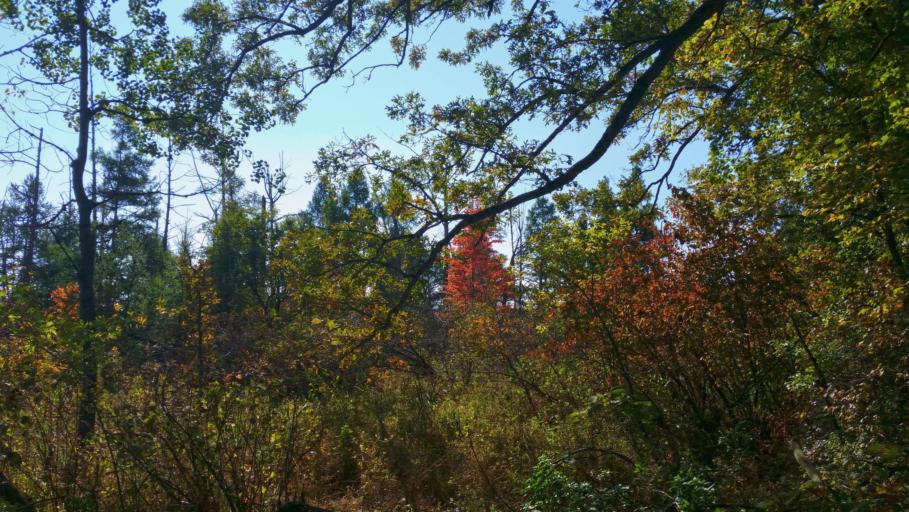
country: US
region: Wisconsin
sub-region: Jefferson County
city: Lake Mills
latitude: 43.0607
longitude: -88.9465
